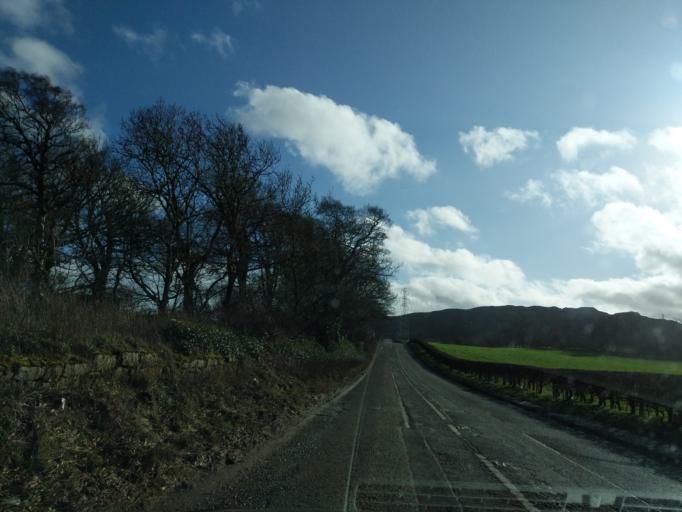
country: GB
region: Scotland
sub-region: Edinburgh
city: Ratho
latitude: 55.8991
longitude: -3.3862
